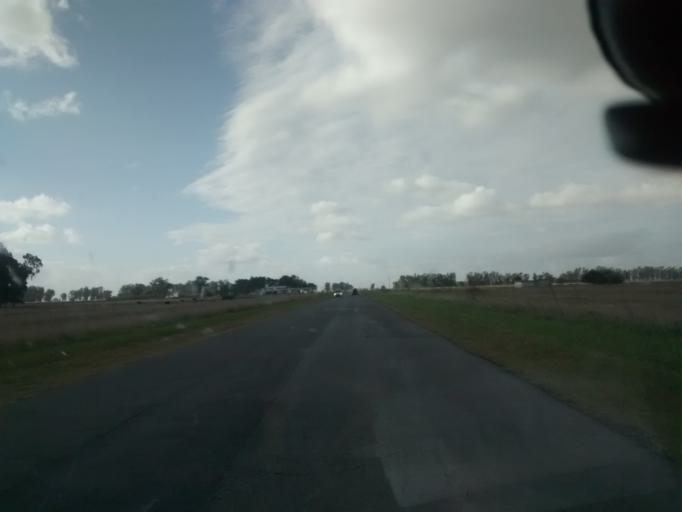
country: AR
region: Buenos Aires
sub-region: Partido de Ayacucho
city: Ayacucho
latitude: -37.1377
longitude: -58.5531
